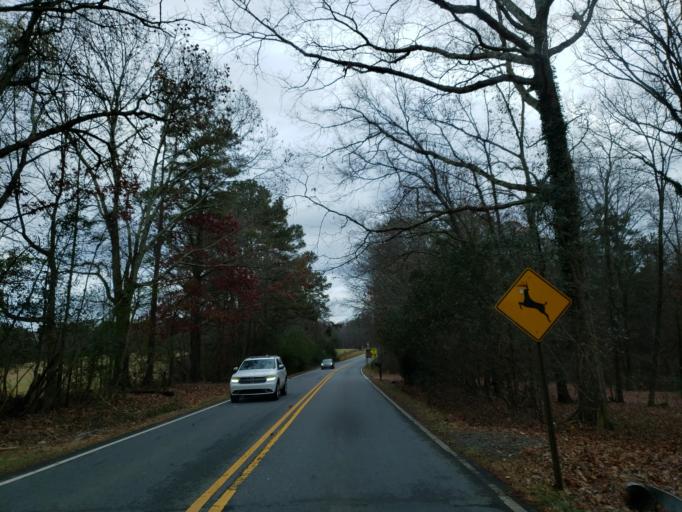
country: US
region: Georgia
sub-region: Cobb County
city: Marietta
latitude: 33.9358
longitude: -84.6057
